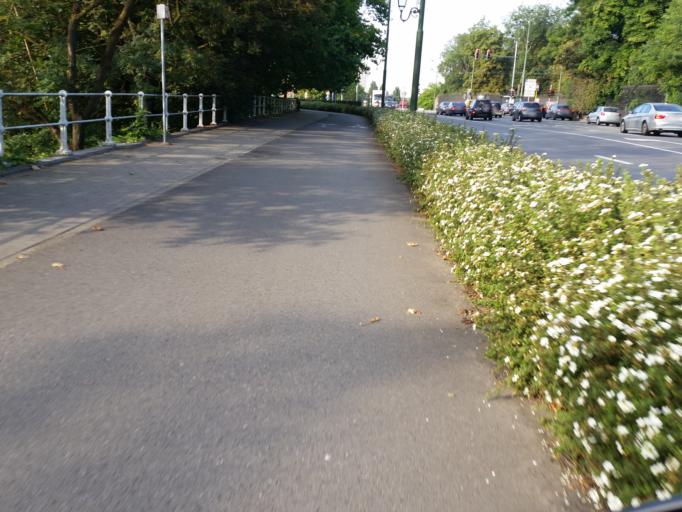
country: BE
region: Brussels Capital
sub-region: Bruxelles-Capitale
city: Brussels
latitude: 50.8824
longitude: 4.3745
